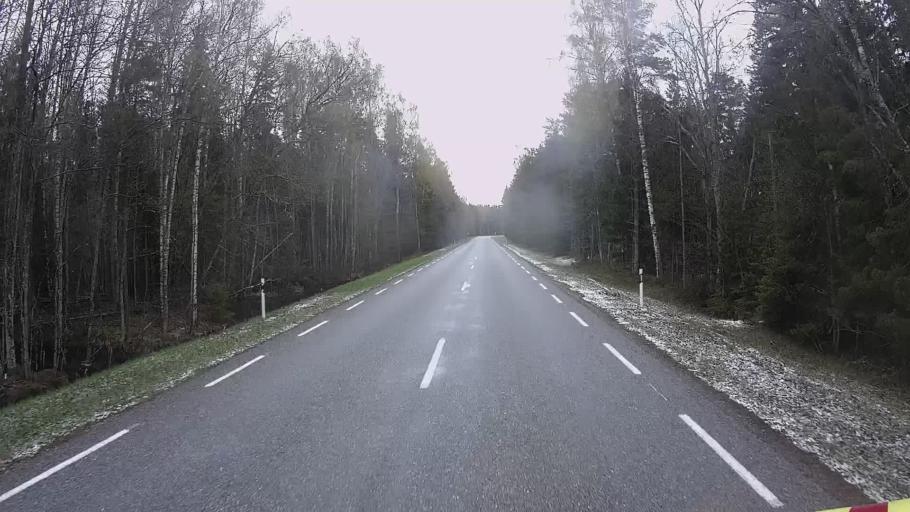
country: EE
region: Hiiumaa
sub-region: Kaerdla linn
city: Kardla
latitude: 59.0417
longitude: 22.6818
